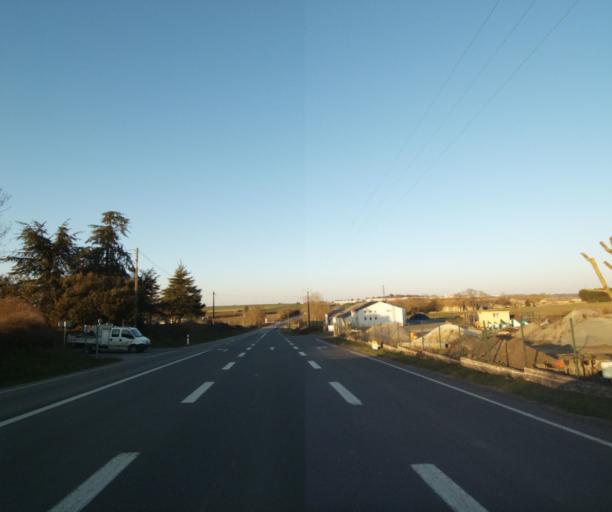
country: FR
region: Poitou-Charentes
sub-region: Departement des Deux-Sevres
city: Niort
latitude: 46.3531
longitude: -0.4397
